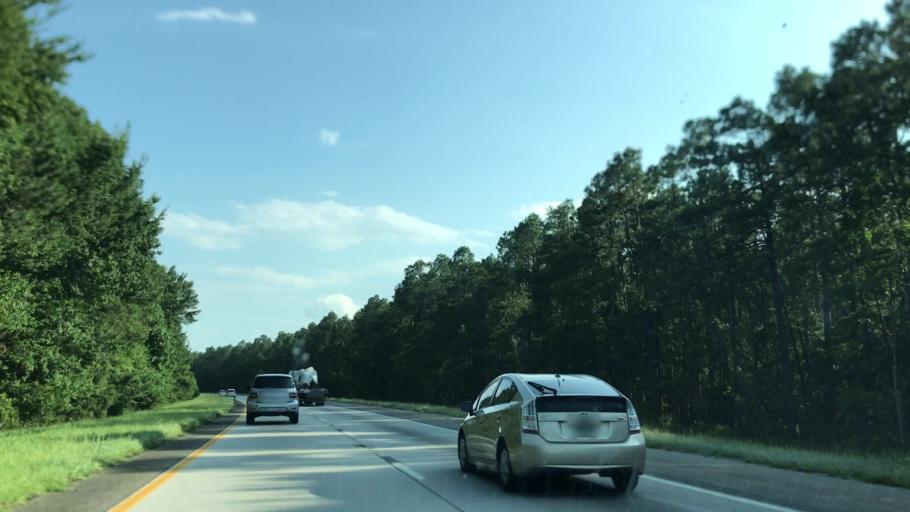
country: US
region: South Carolina
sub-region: Colleton County
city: Walterboro
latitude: 33.0489
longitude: -80.6689
